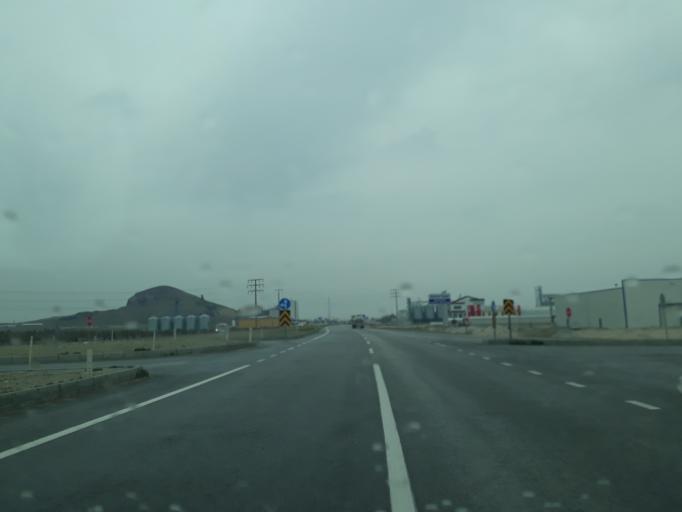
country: TR
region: Konya
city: Karapinar
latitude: 37.7137
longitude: 33.5937
